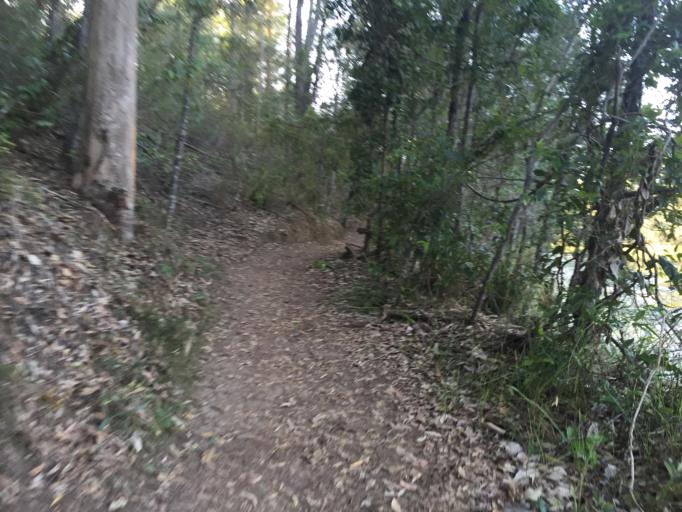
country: AU
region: Queensland
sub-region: Moreton Bay
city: Ferny Hills
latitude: -27.4412
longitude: 152.9225
